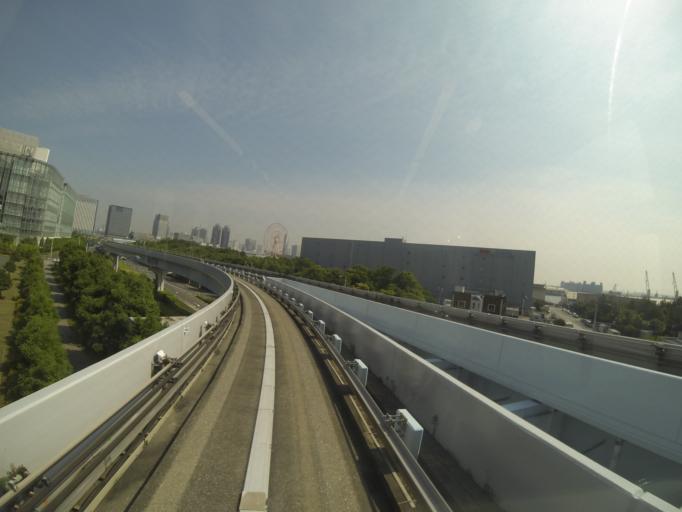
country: JP
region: Tokyo
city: Tokyo
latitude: 35.6175
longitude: 139.7819
